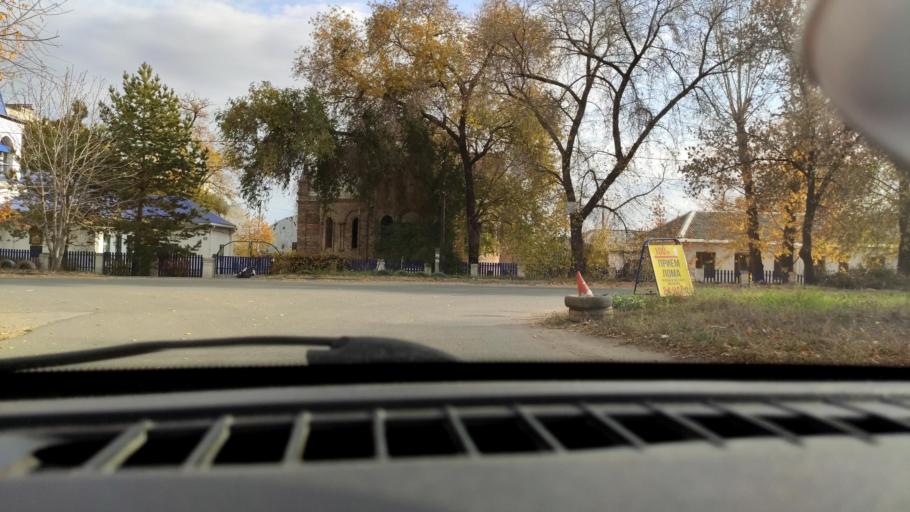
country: RU
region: Samara
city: Samara
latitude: 53.1882
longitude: 50.2120
